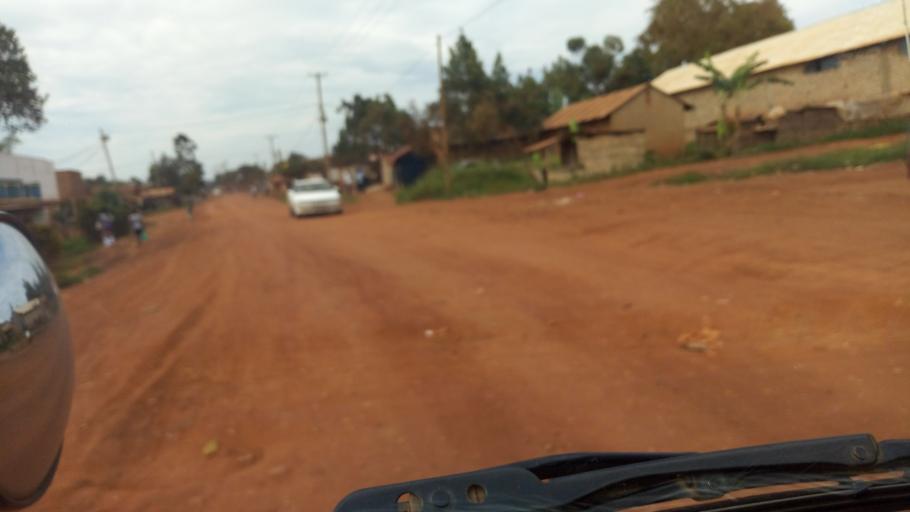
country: UG
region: Central Region
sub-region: Wakiso District
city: Bweyogerere
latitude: 0.3590
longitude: 32.7022
